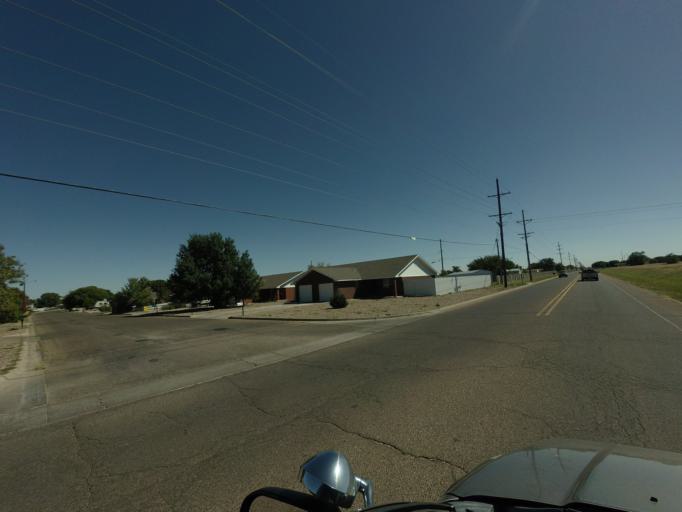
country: US
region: New Mexico
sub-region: Curry County
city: Clovis
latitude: 34.4161
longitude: -103.2318
